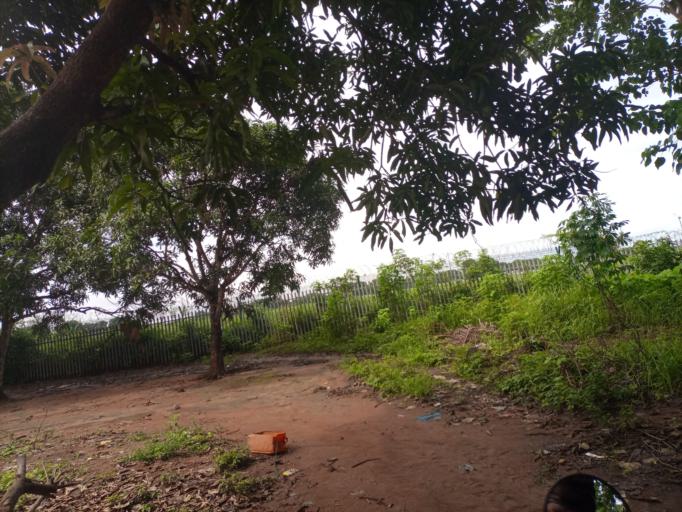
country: SL
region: Northern Province
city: Tintafor
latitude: 8.6220
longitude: -13.2081
